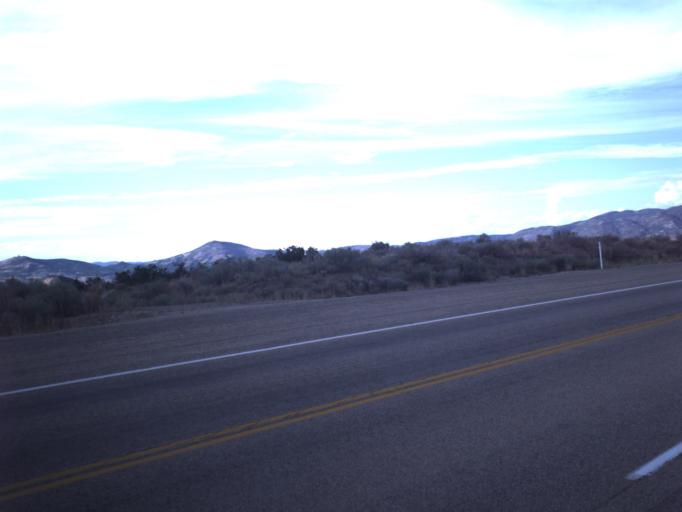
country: US
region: Utah
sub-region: Wasatch County
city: Heber
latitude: 40.5913
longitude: -111.4211
